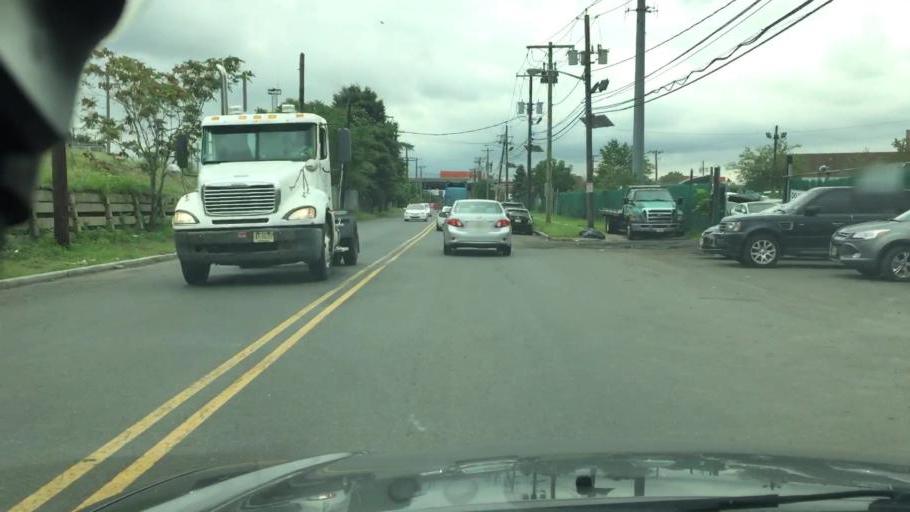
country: US
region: New Jersey
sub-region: Union County
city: Elizabeth
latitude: 40.6604
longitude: -74.1912
